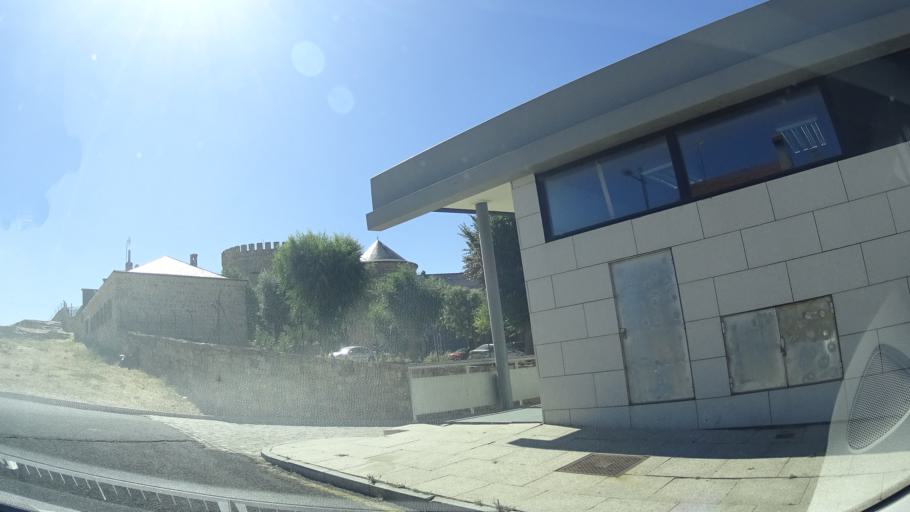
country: ES
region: Castille and Leon
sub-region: Provincia de Avila
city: Las Navas del Marques
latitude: 40.6045
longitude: -4.3263
